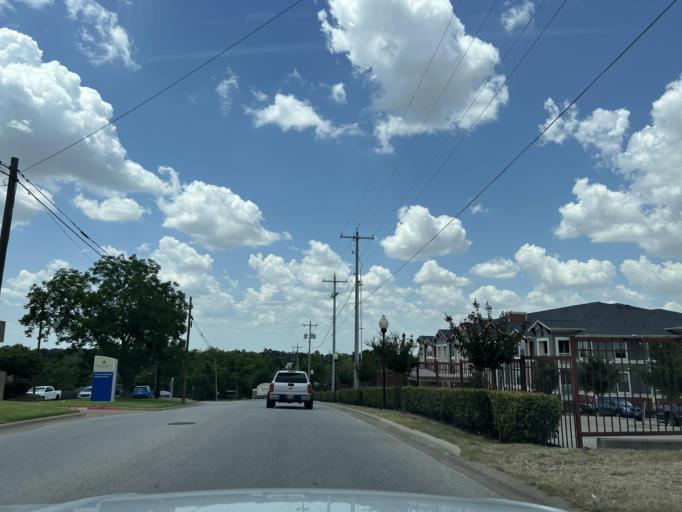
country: US
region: Texas
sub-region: Washington County
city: Brenham
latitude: 30.1712
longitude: -96.3973
